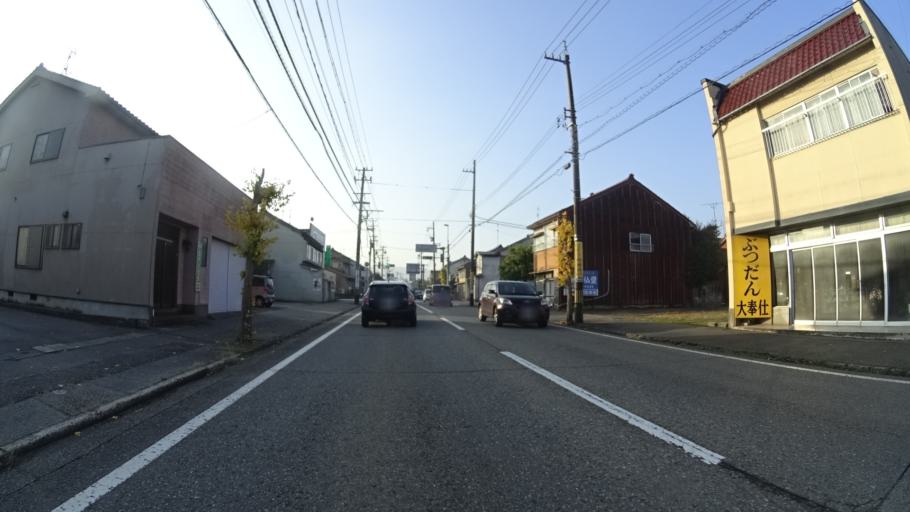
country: JP
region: Ishikawa
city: Nanao
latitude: 37.0401
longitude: 136.9693
